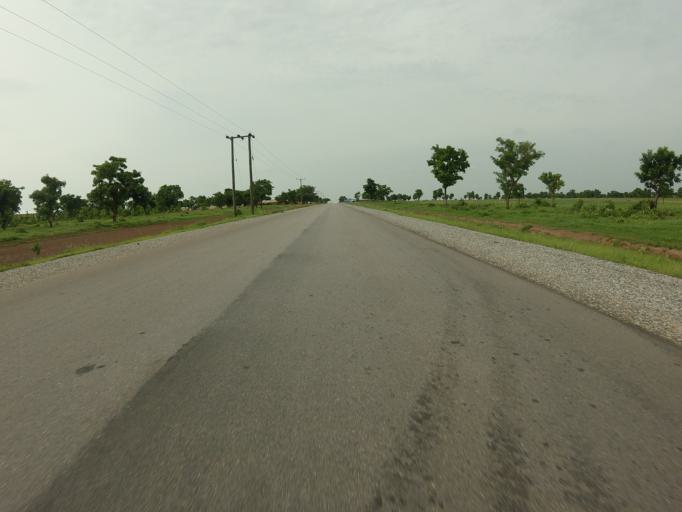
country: GH
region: Northern
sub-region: Yendi
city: Yendi
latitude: 9.8158
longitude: -0.1167
